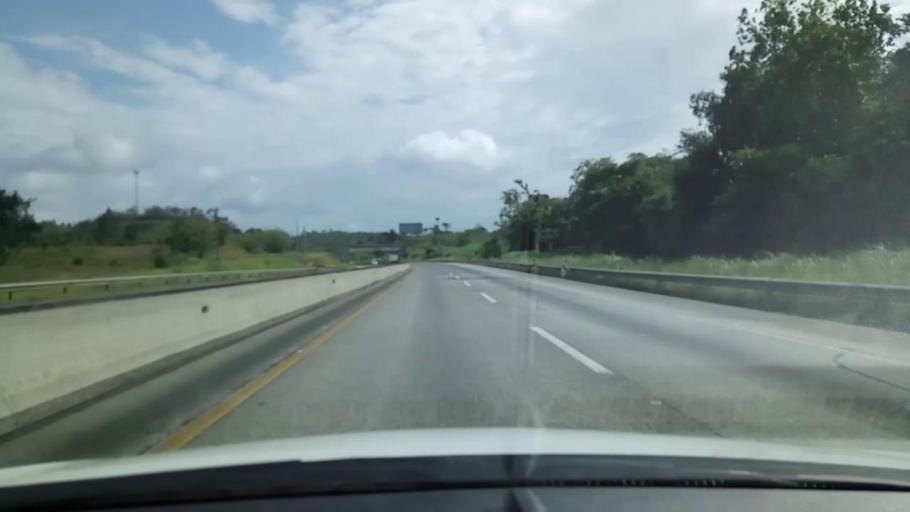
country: PA
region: Colon
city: El Giral
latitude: 9.2545
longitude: -79.6918
